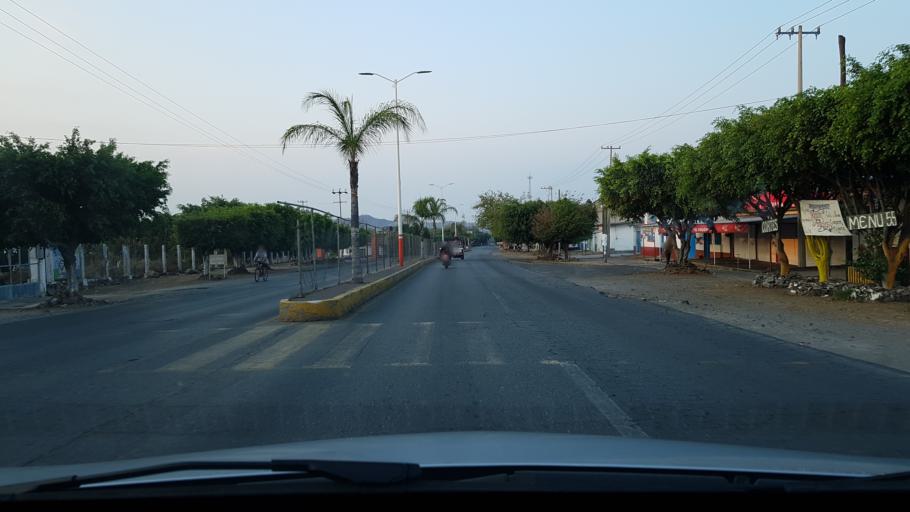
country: MX
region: Morelos
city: Jonacatepec de Leandro Valle
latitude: 18.6921
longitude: -98.8018
